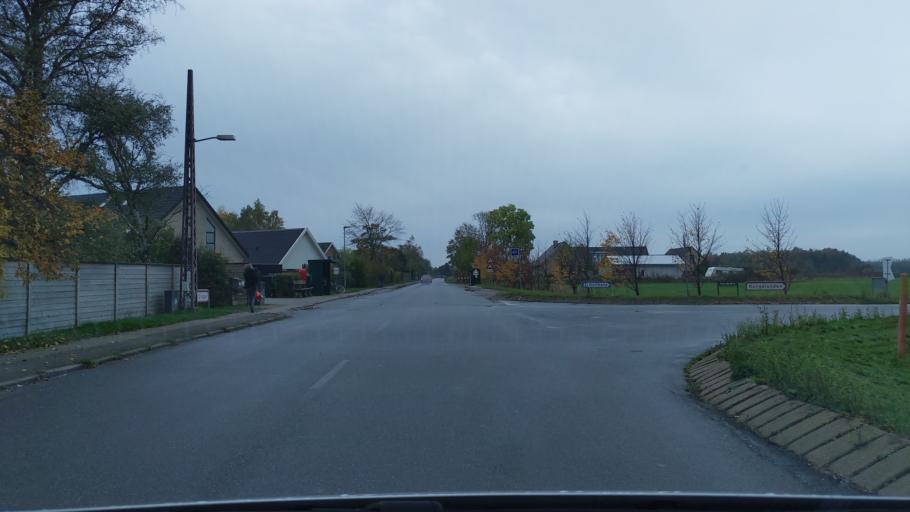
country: DK
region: Capital Region
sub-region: Dragor Kommune
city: Dragor
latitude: 55.5742
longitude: 12.6167
